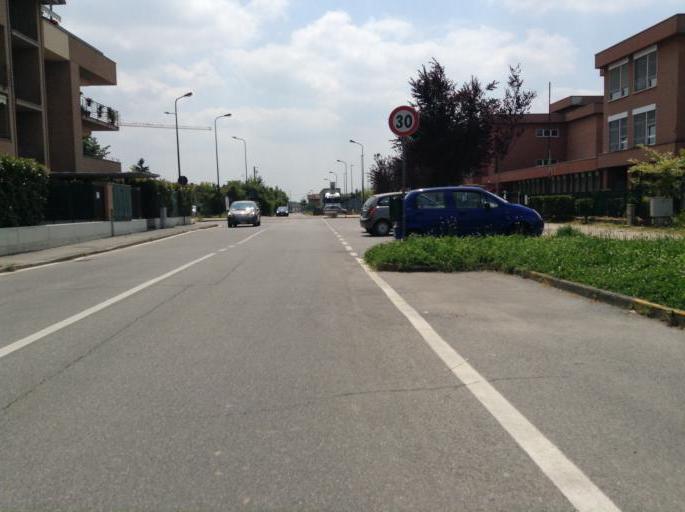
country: IT
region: Piedmont
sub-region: Provincia di Torino
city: Carignano
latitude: 44.9072
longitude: 7.6695
